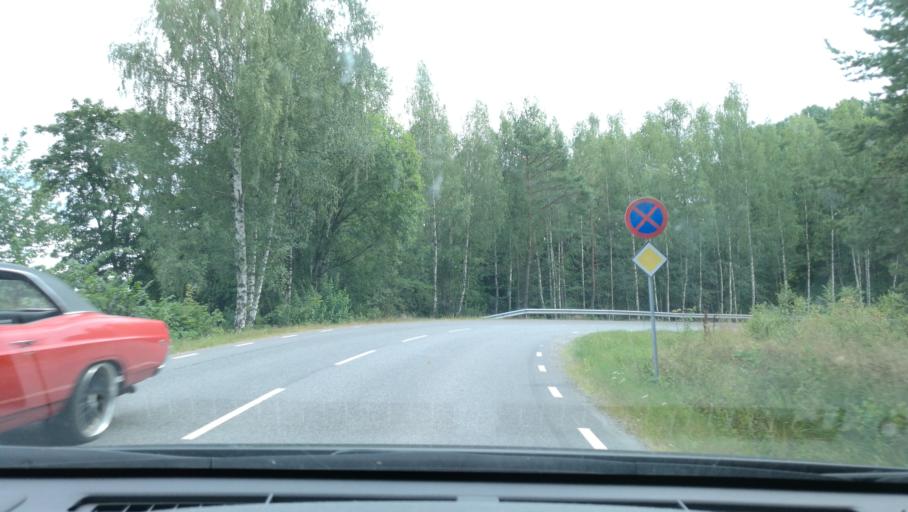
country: SE
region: OEstergoetland
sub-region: Norrkopings Kommun
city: Krokek
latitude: 58.6621
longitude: 16.4052
